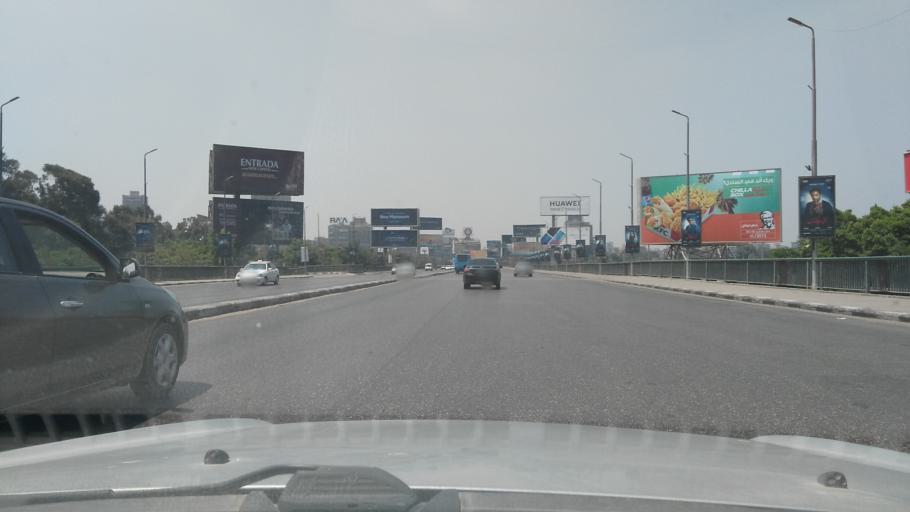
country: EG
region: Muhafazat al Qahirah
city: Cairo
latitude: 30.0493
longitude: 31.2272
